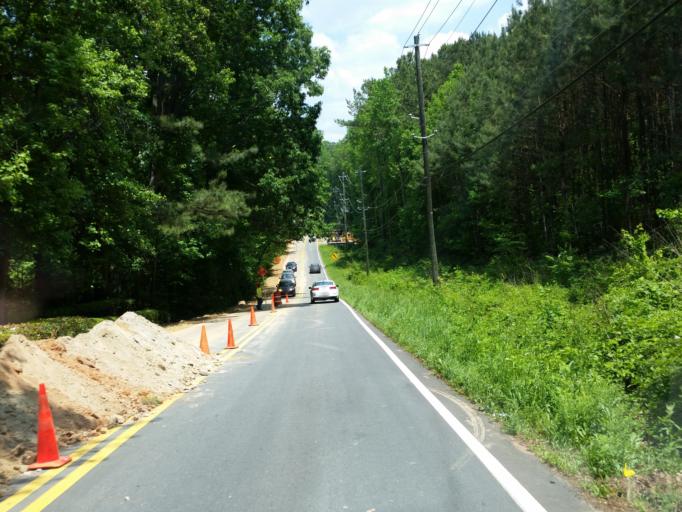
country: US
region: Georgia
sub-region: Cobb County
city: Vinings
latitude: 33.8743
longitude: -84.4771
